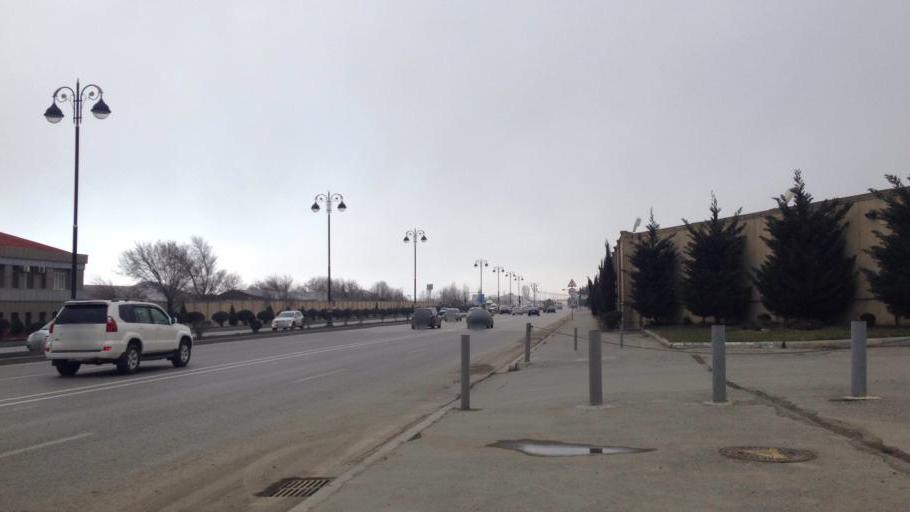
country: AZ
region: Baki
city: Baku
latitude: 40.3773
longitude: 49.9062
